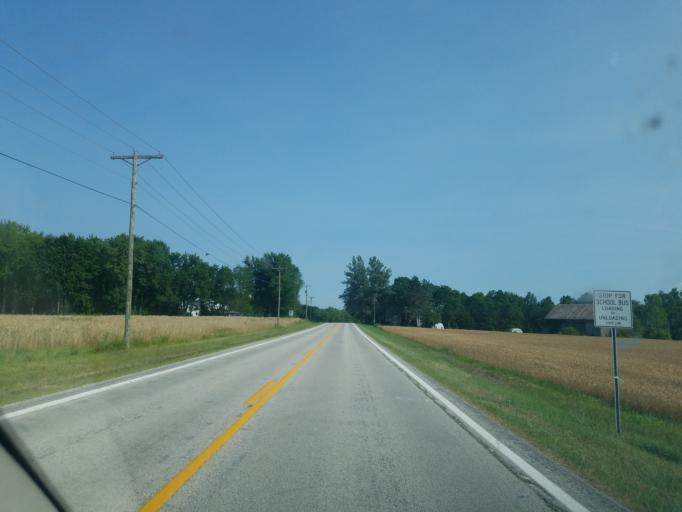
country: US
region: Ohio
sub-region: Wyandot County
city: Carey
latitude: 40.9953
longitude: -83.2682
